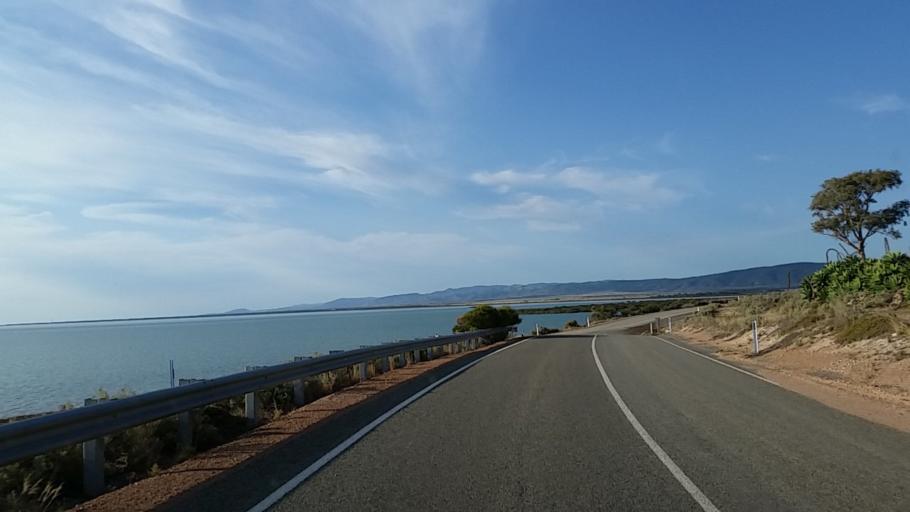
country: AU
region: South Australia
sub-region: Port Pirie City and Dists
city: Port Pirie
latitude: -33.1032
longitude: 138.0248
